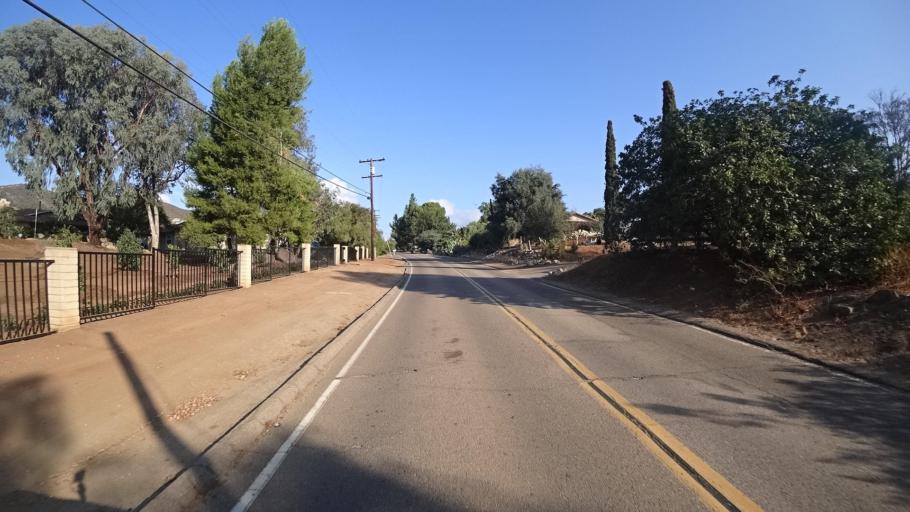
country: US
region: California
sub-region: San Diego County
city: Eucalyptus Hills
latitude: 32.8792
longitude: -116.9527
